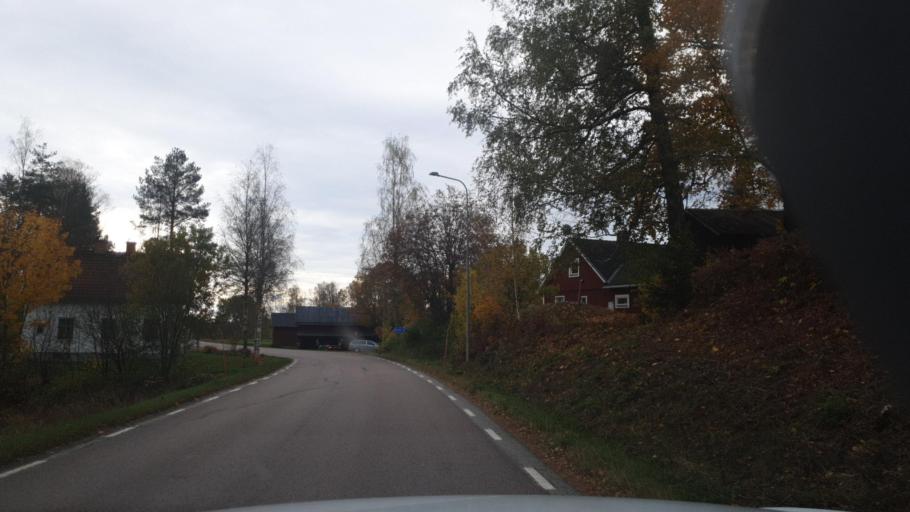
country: SE
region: Vaermland
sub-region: Arvika Kommun
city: Arvika
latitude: 59.6881
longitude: 12.7877
